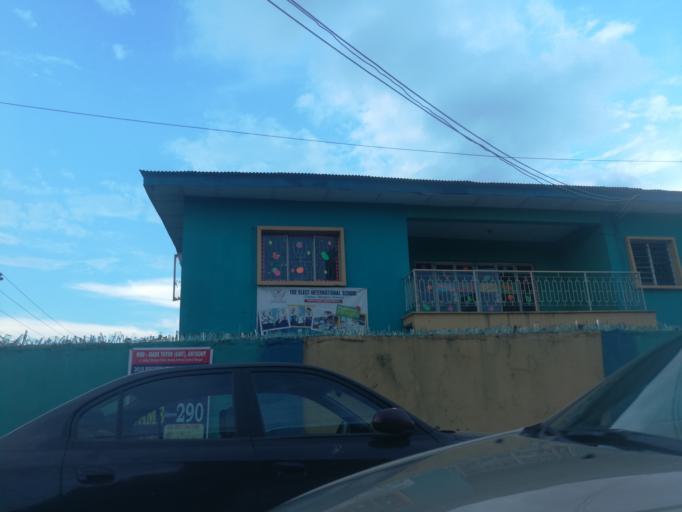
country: NG
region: Lagos
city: Somolu
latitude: 6.5607
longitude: 3.3702
